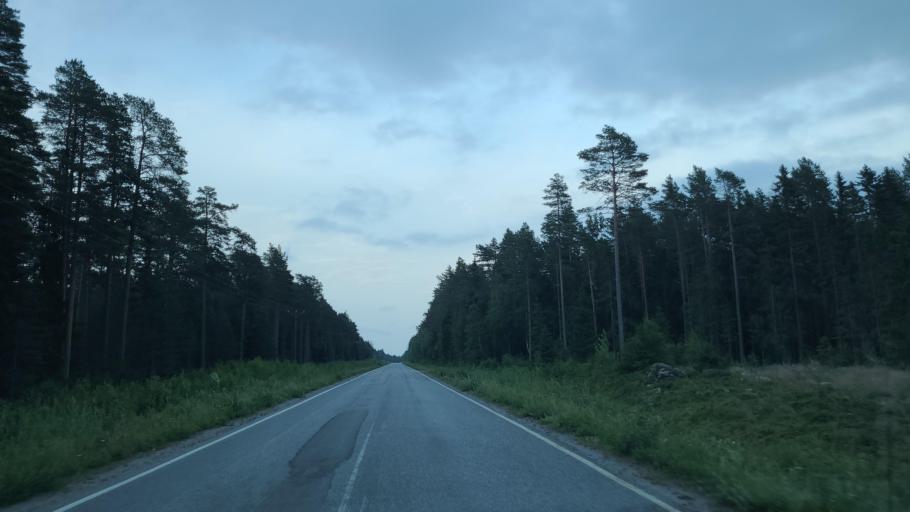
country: FI
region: Ostrobothnia
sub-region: Vaasa
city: Replot
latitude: 63.2033
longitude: 21.2765
